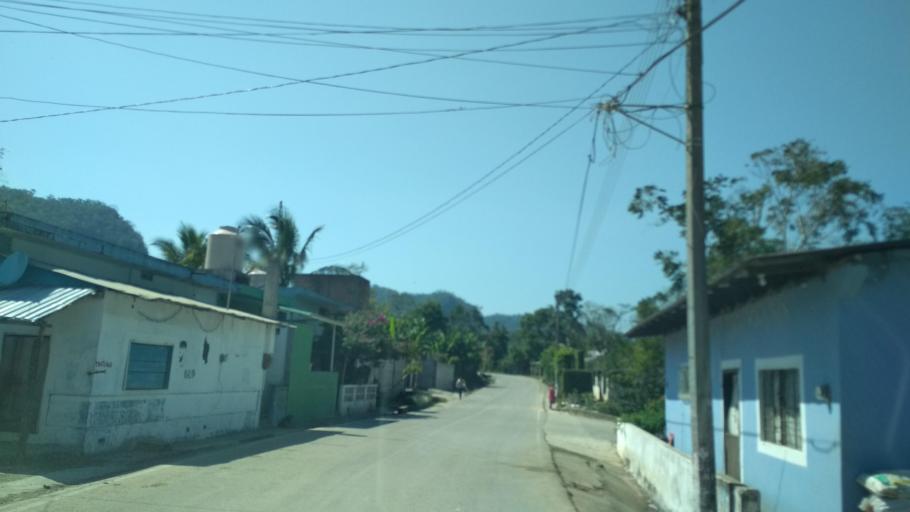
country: MX
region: Veracruz
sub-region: Papantla
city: Polutla
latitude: 20.4759
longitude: -97.2087
